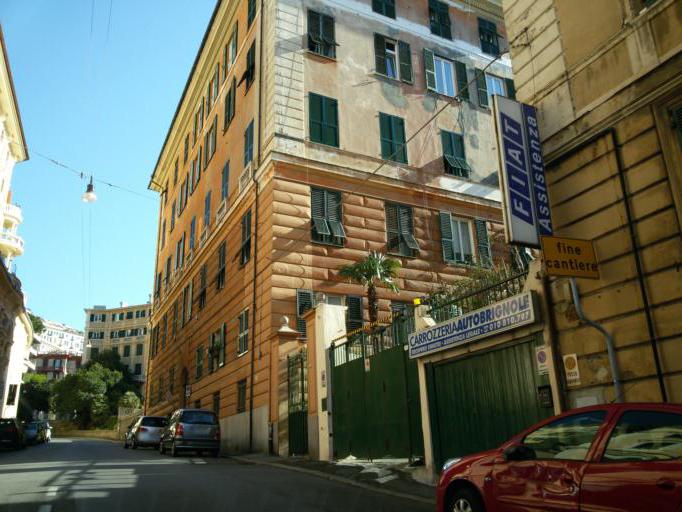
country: IT
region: Liguria
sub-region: Provincia di Genova
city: Genoa
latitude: 44.4094
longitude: 8.9438
